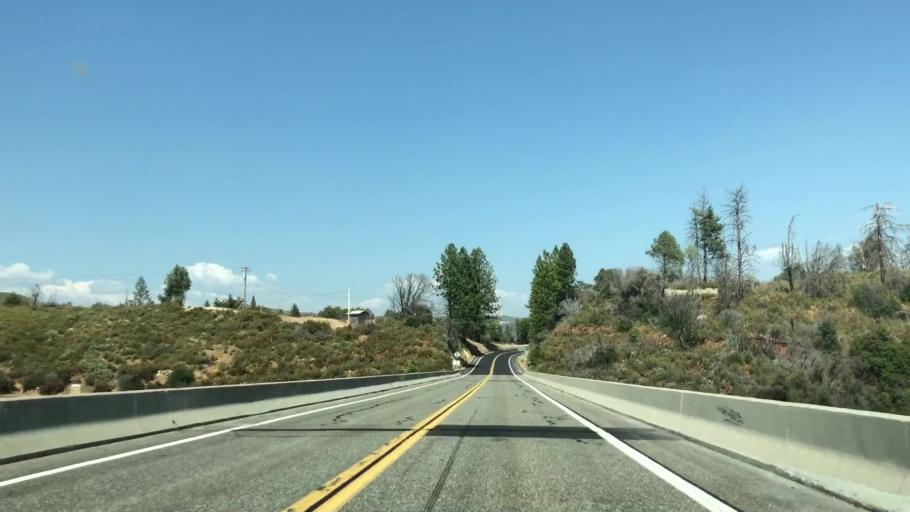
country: US
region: California
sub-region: Tuolumne County
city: Tuolumne City
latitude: 37.8231
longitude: -120.0139
